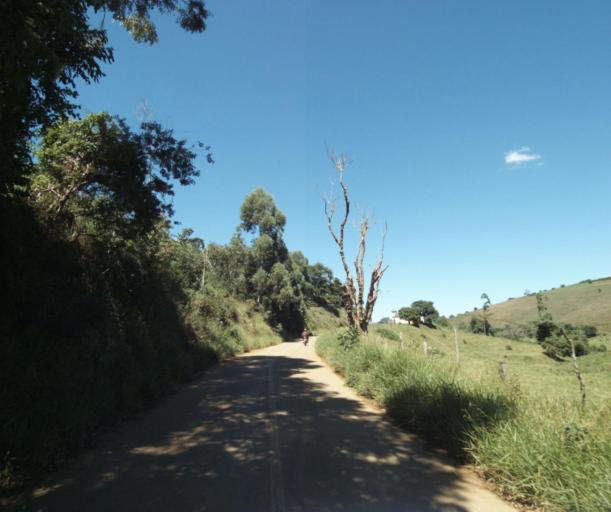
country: BR
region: Minas Gerais
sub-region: Espera Feliz
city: Espera Feliz
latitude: -20.5922
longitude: -41.8383
